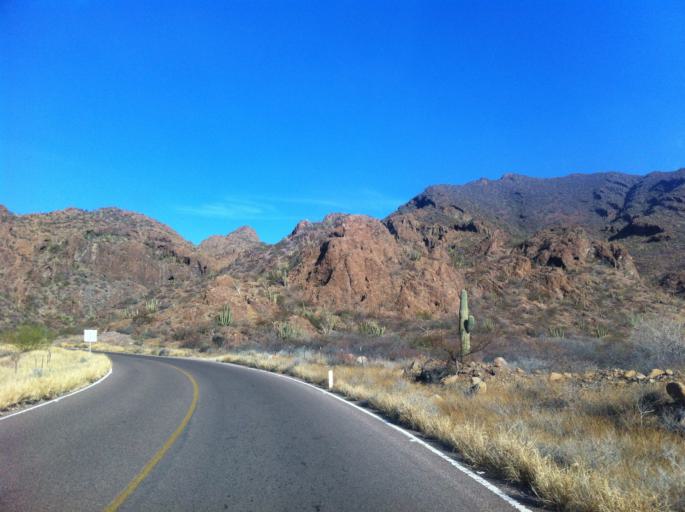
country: MX
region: Sonora
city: Heroica Guaymas
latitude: 27.9268
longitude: -110.9580
